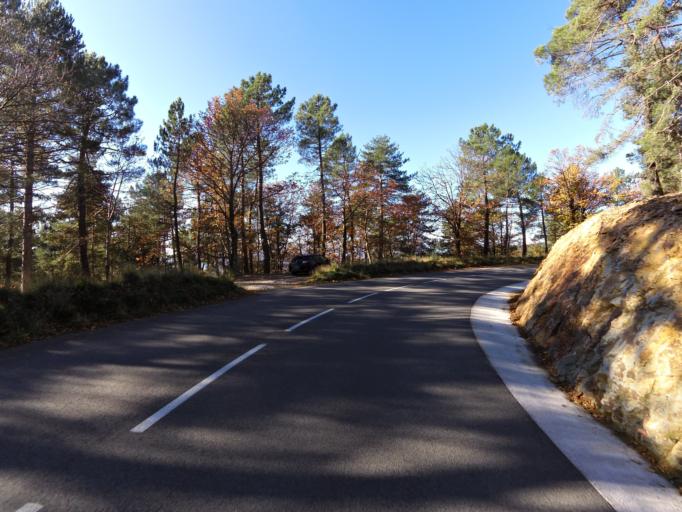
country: FR
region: Rhone-Alpes
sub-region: Departement de l'Ardeche
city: Les Vans
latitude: 44.4992
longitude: 4.1261
